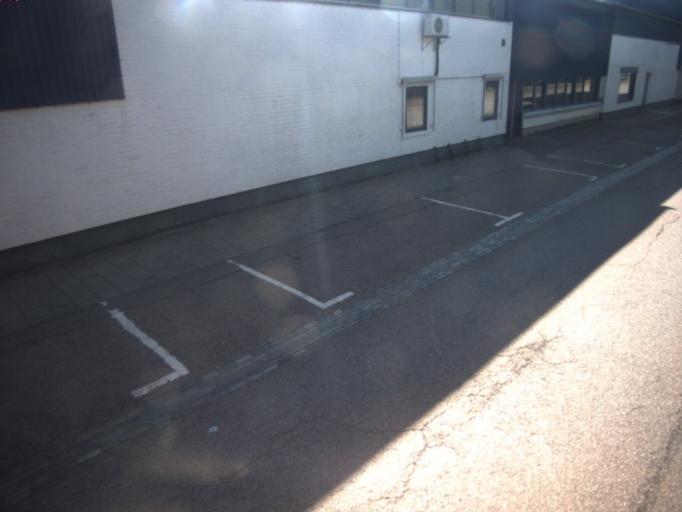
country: SE
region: Skane
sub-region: Helsingborg
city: Helsingborg
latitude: 56.0248
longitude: 12.7148
